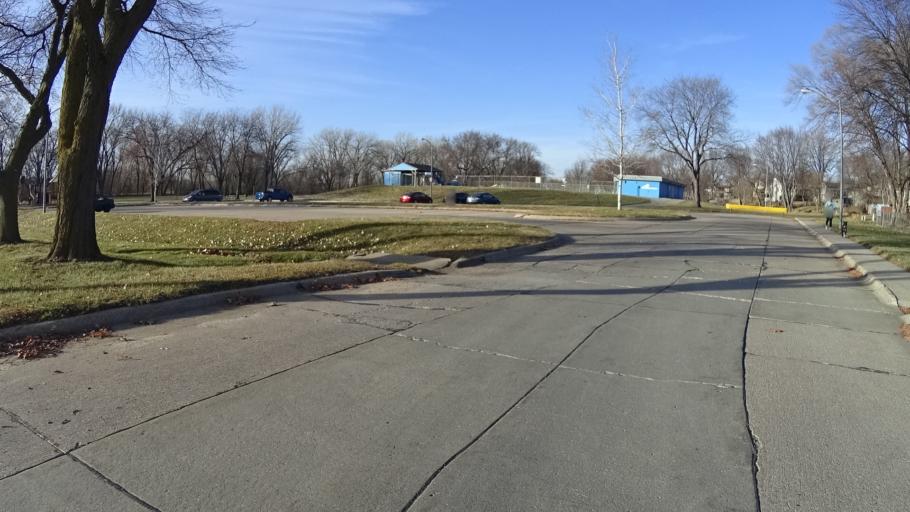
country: US
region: Nebraska
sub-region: Sarpy County
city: La Vista
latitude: 41.1847
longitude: -95.9986
